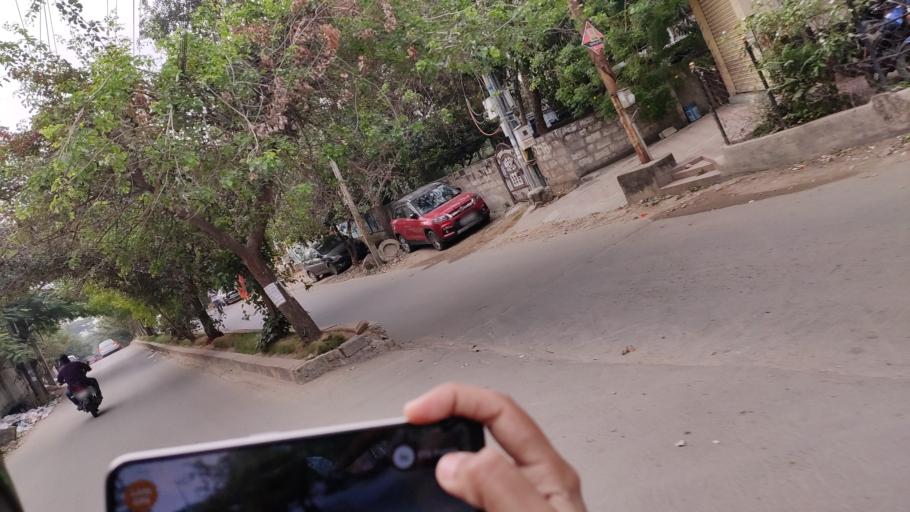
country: IN
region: Telangana
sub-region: Rangareddi
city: Kukatpalli
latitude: 17.4905
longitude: 78.3860
